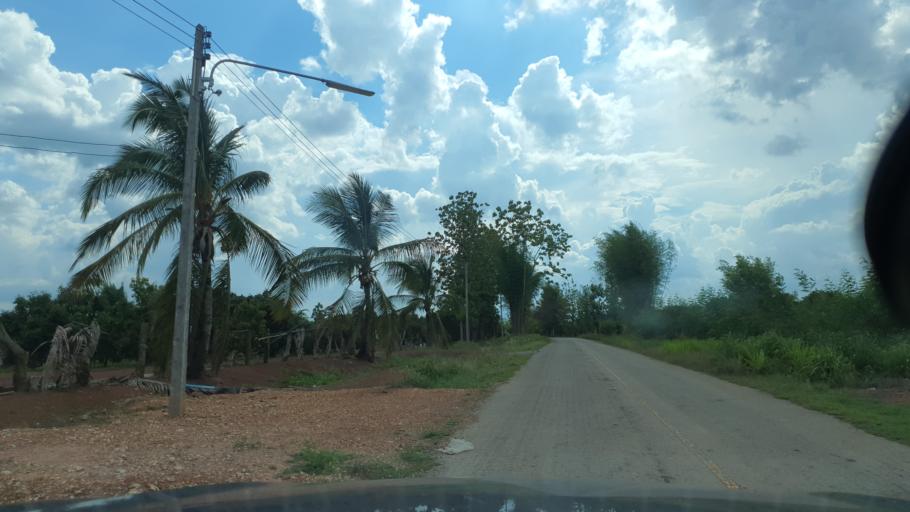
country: TH
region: Chiang Mai
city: Mae Taeng
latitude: 19.1312
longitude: 99.0435
